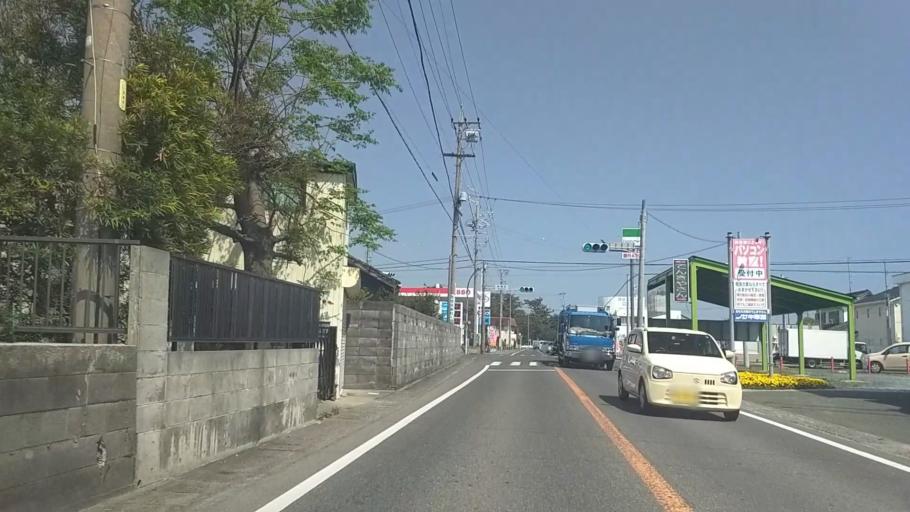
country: JP
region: Shizuoka
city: Hamamatsu
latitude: 34.6804
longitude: 137.7086
